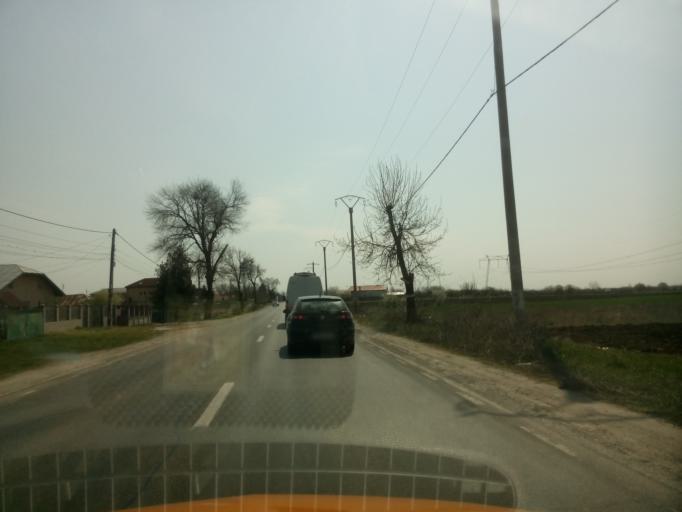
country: RO
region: Calarasi
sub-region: Comuna Frumusani
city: Frumusani
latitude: 44.3090
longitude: 26.2923
